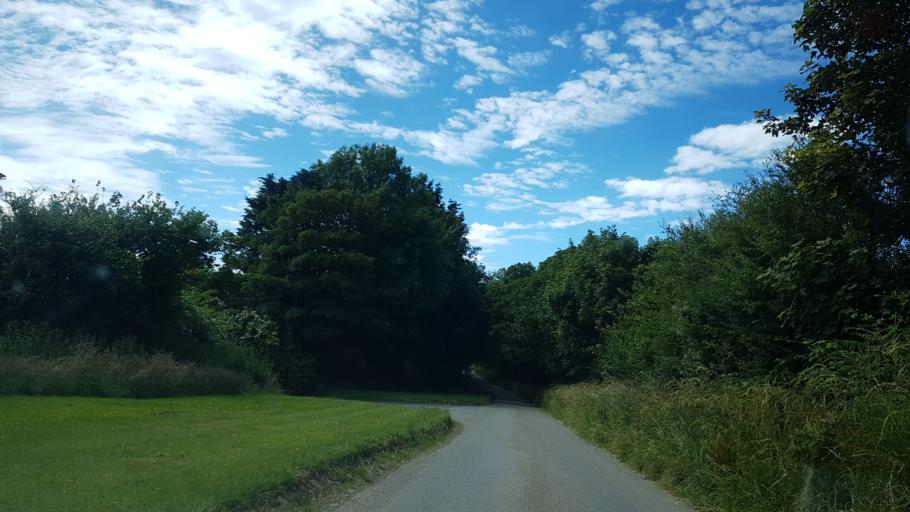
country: GB
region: Wales
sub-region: Pembrokeshire
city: Wiston
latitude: 51.8280
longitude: -4.8825
